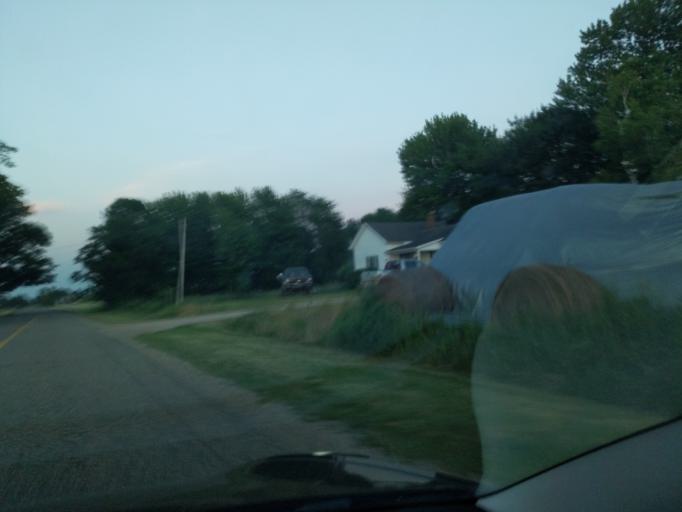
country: US
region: Michigan
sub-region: Eaton County
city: Bellevue
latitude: 42.5385
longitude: -84.9953
